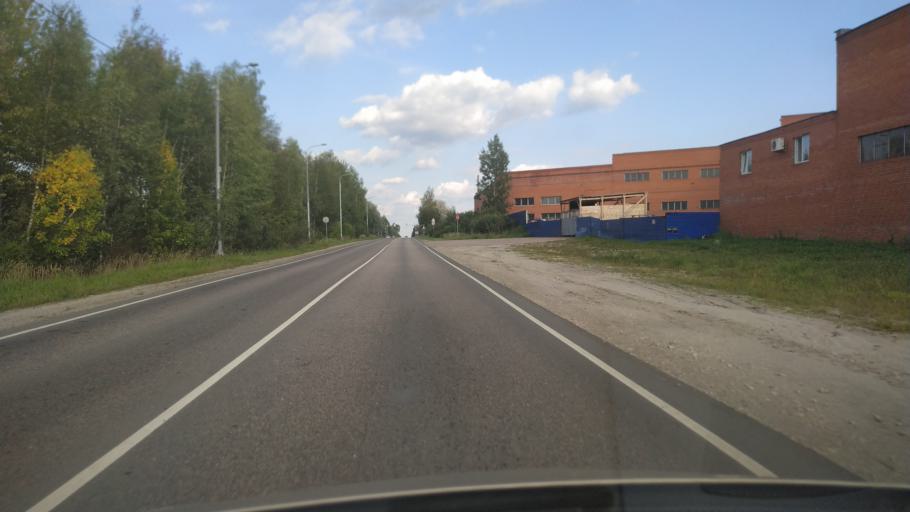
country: RU
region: Moskovskaya
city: Vereya
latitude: 55.7083
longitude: 39.1044
